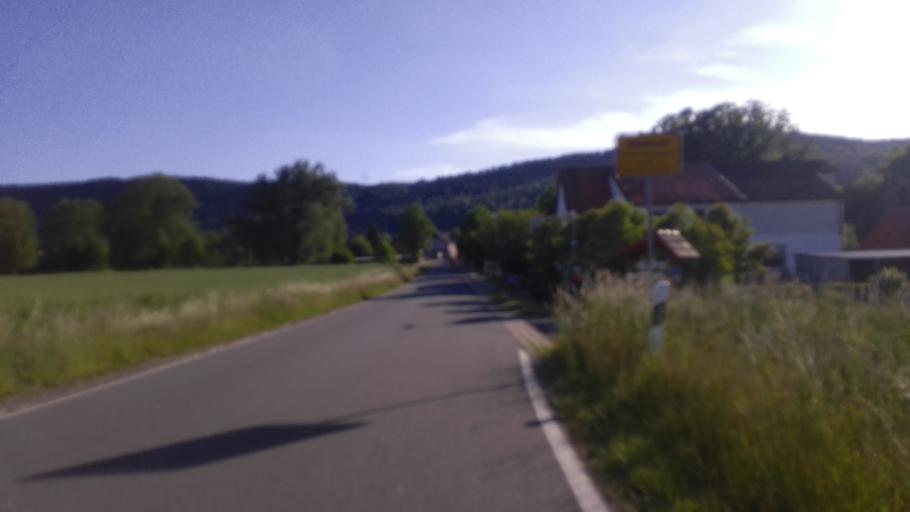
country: DE
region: Lower Saxony
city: Salzhemmendorf
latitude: 52.0321
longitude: 9.6060
